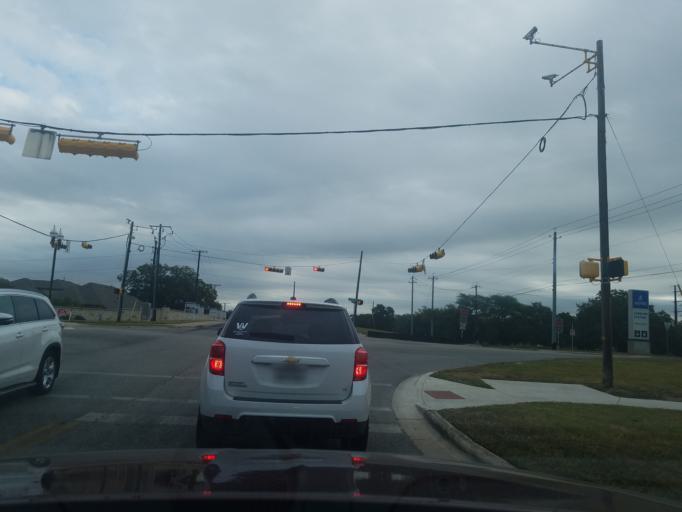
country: US
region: Texas
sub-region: Williamson County
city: Anderson Mill
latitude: 30.4819
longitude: -97.7899
